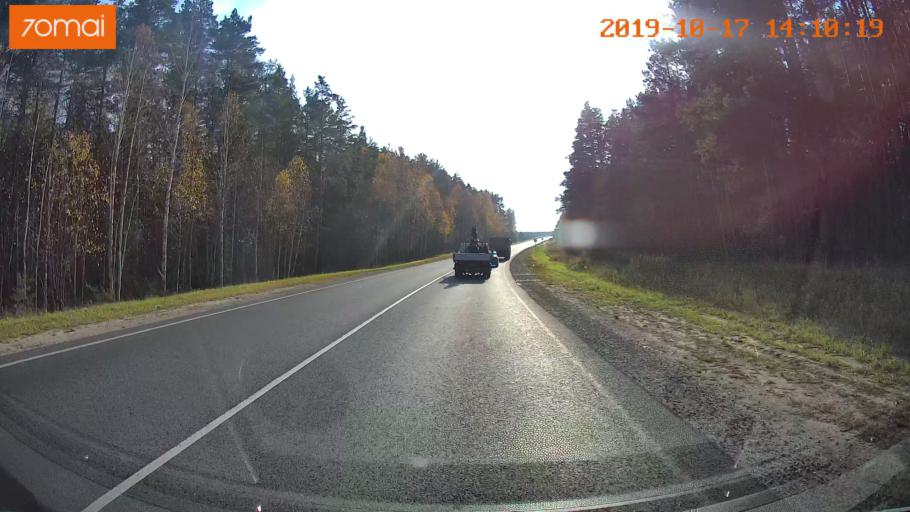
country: RU
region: Rjazan
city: Spas-Klepiki
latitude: 55.0802
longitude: 40.0517
